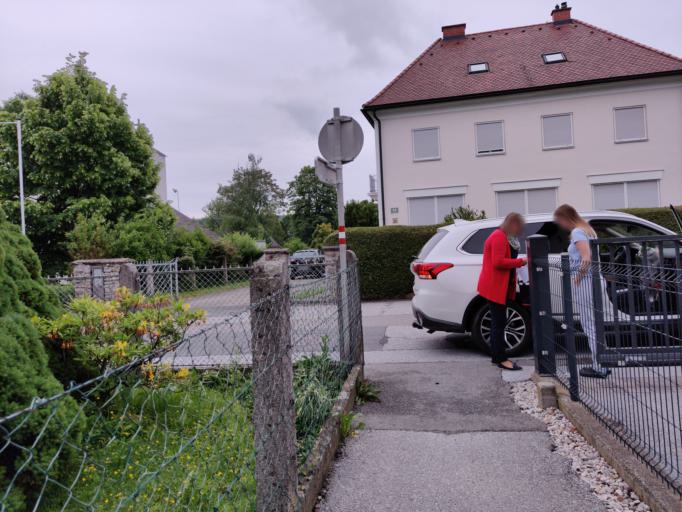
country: AT
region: Styria
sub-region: Politischer Bezirk Deutschlandsberg
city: Deutschlandsberg
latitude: 46.8167
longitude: 15.2193
